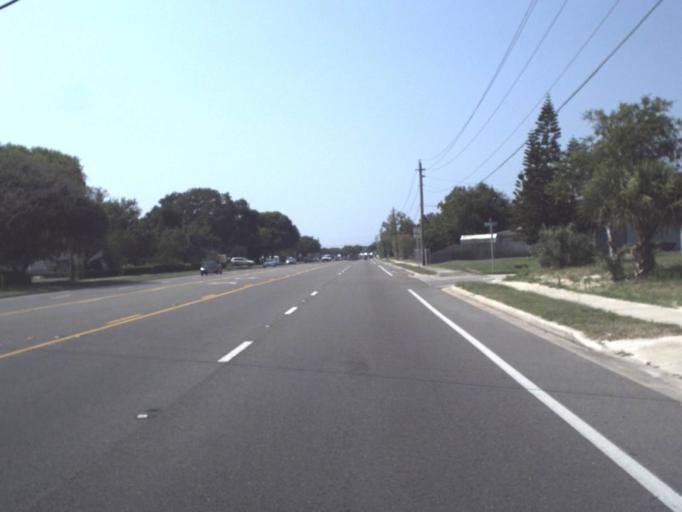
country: US
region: Florida
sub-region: Saint Johns County
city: Saint Augustine Beach
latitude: 29.8692
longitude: -81.2836
